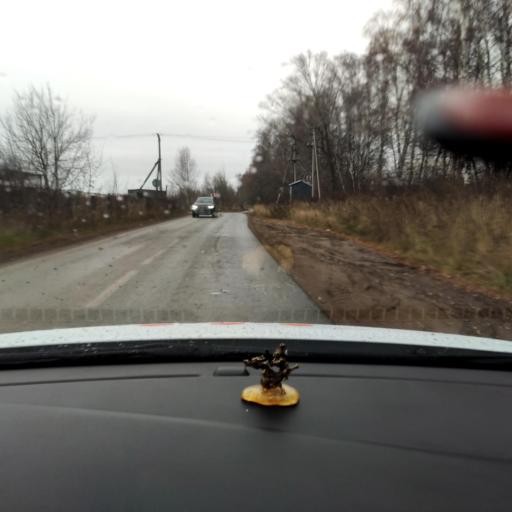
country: RU
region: Tatarstan
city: Vysokaya Gora
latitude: 55.8258
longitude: 49.2409
